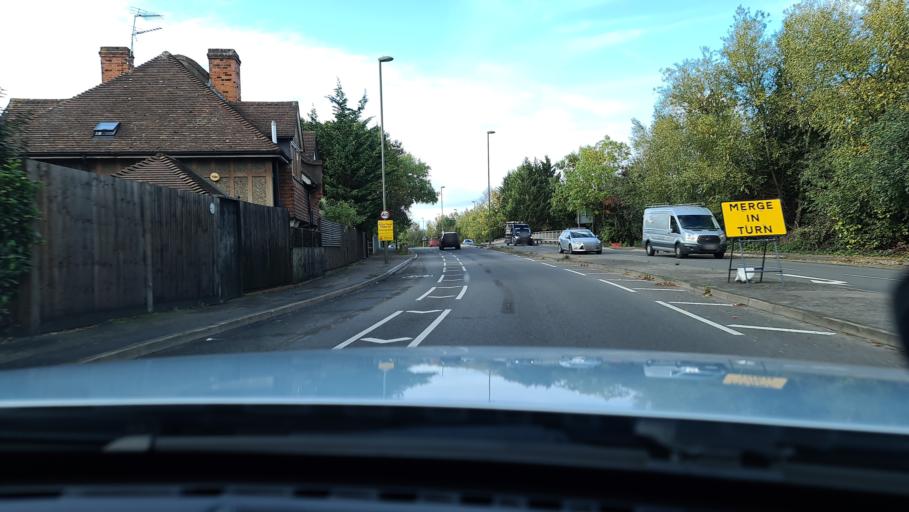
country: GB
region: England
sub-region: Surrey
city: Esher
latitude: 51.3679
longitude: -0.3776
